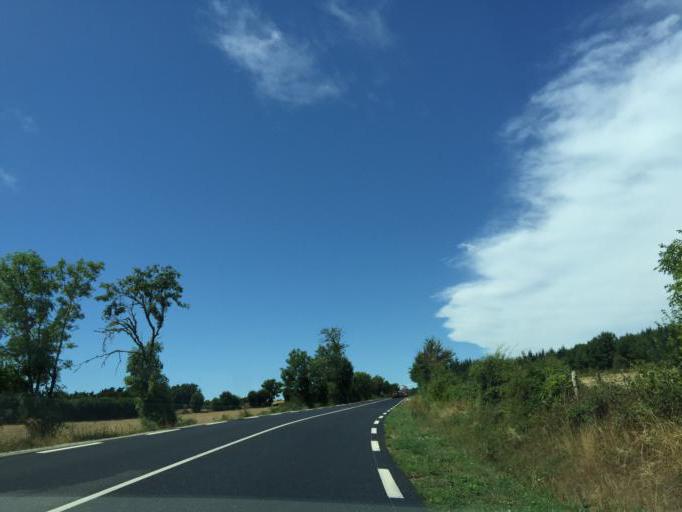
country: FR
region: Midi-Pyrenees
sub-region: Departement de l'Aveyron
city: Severac-le-Chateau
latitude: 44.2360
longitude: 2.9758
